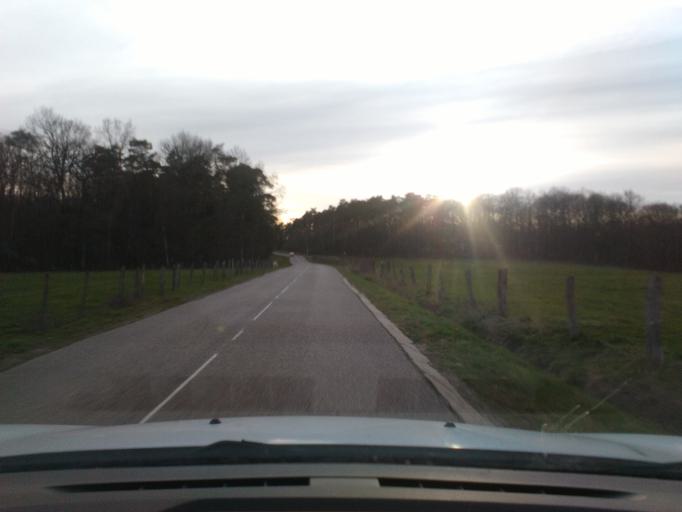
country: FR
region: Lorraine
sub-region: Departement des Vosges
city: Chatel-sur-Moselle
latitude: 48.3540
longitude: 6.4540
